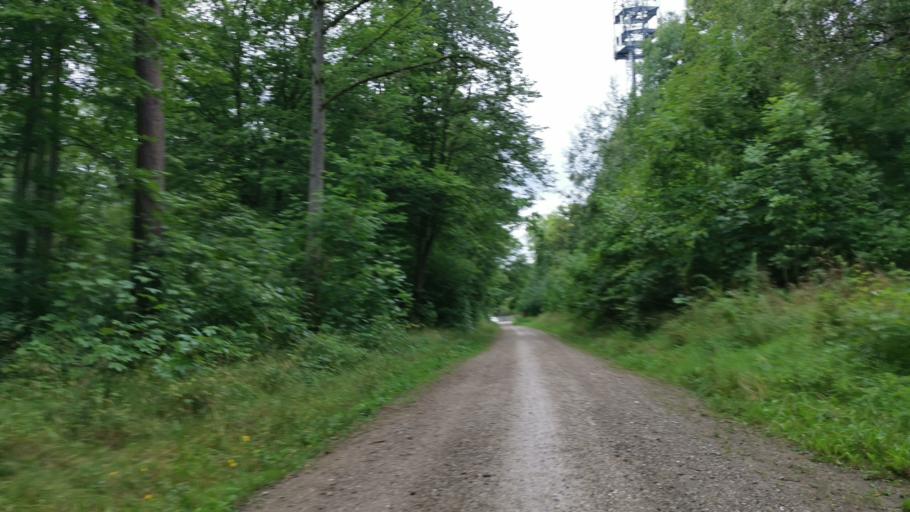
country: DE
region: Bavaria
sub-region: Upper Bavaria
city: Pullach im Isartal
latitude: 48.0775
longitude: 11.5528
